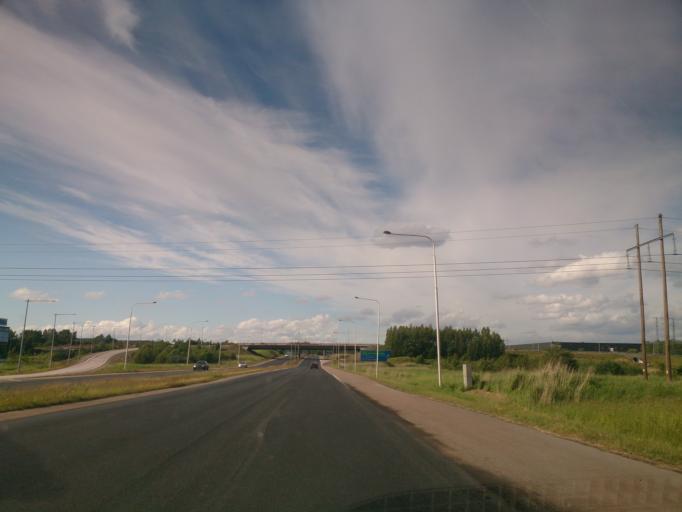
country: SE
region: OEstergoetland
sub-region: Norrkopings Kommun
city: Norrkoping
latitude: 58.6234
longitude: 16.1591
